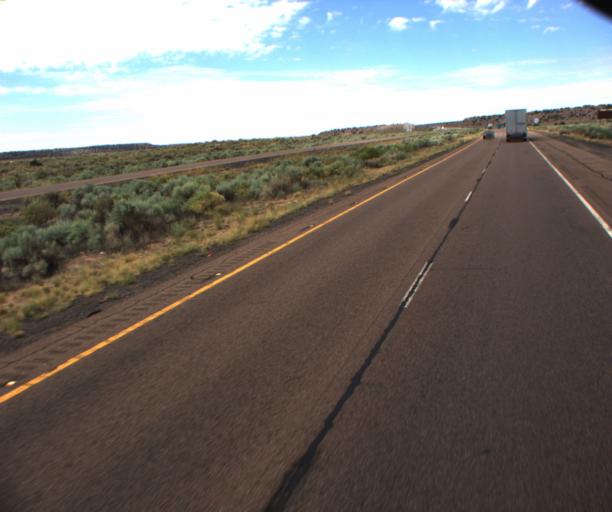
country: US
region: Arizona
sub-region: Apache County
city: Houck
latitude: 35.1883
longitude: -109.4438
